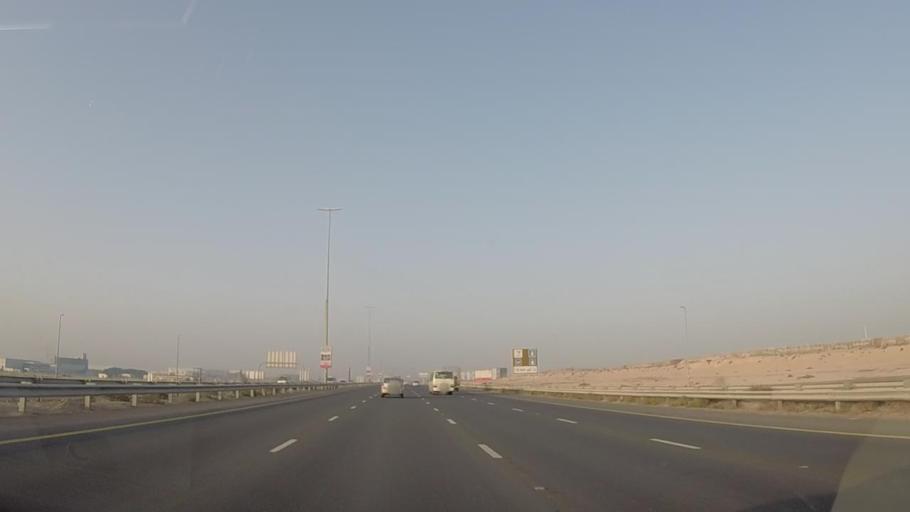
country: AE
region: Dubai
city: Dubai
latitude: 24.9453
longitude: 55.0572
